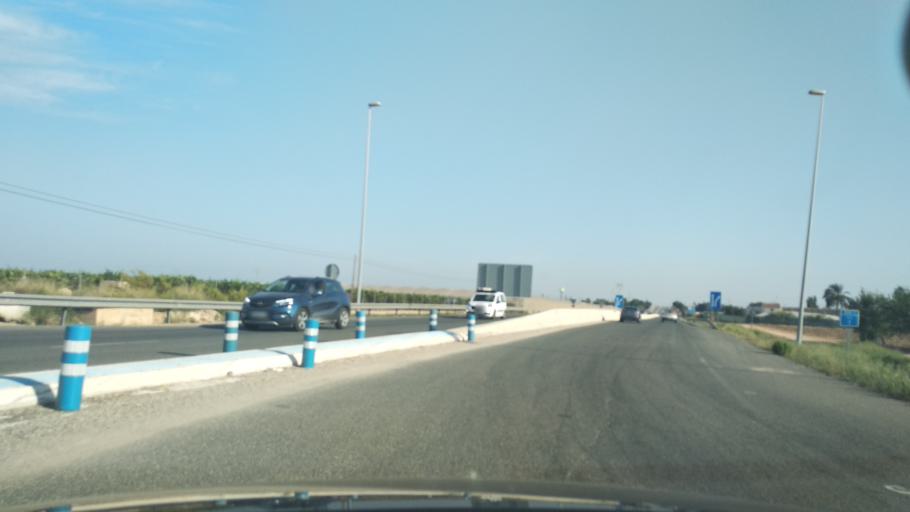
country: ES
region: Murcia
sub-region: Murcia
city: San Javier
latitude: 37.8209
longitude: -0.8488
